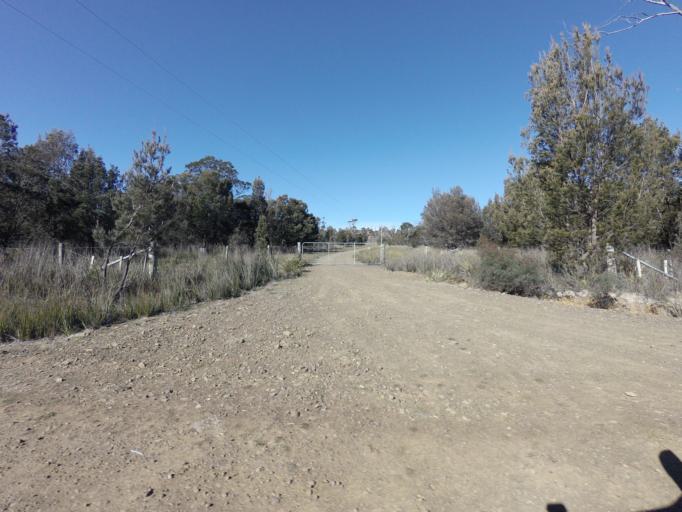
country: AU
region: Tasmania
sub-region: Sorell
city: Sorell
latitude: -42.3480
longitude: 147.9736
